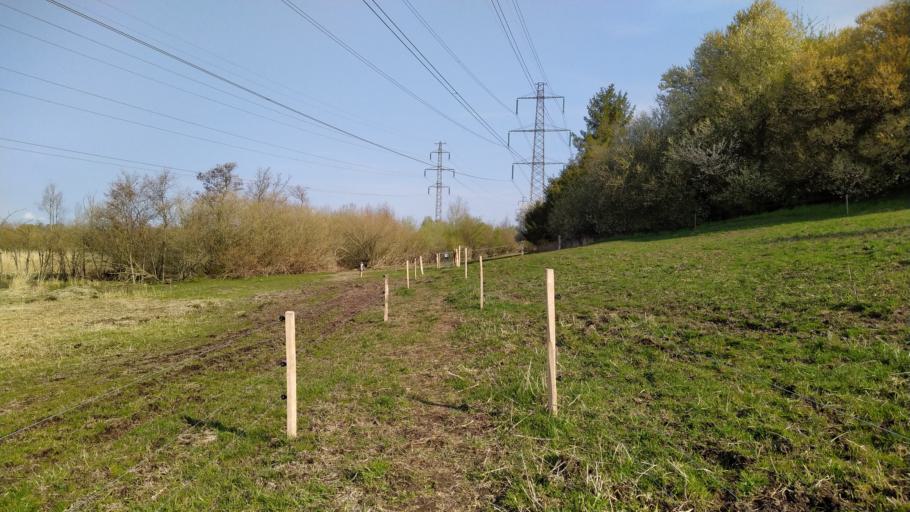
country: DK
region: Capital Region
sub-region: Egedal Kommune
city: Stenlose
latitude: 55.7507
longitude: 12.2140
